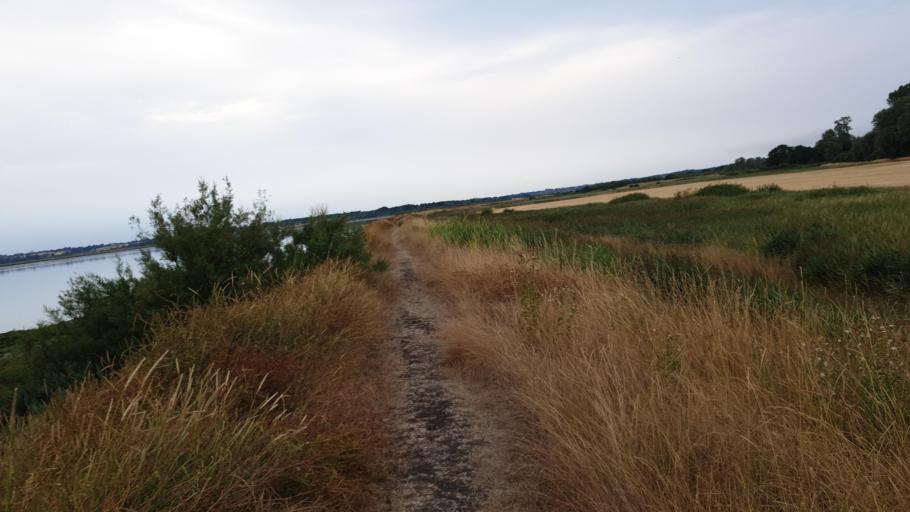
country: GB
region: England
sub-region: Essex
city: Brightlingsea
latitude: 51.8195
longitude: 0.9921
